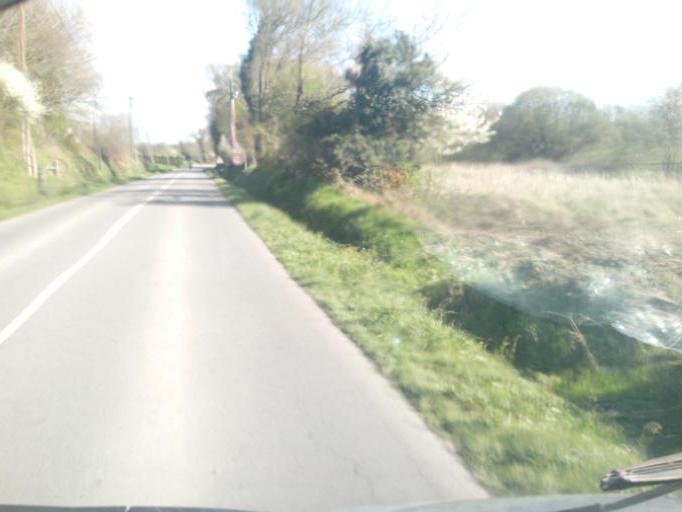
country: FR
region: Brittany
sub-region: Departement d'Ille-et-Vilaine
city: Guipry
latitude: 47.8456
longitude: -1.8649
